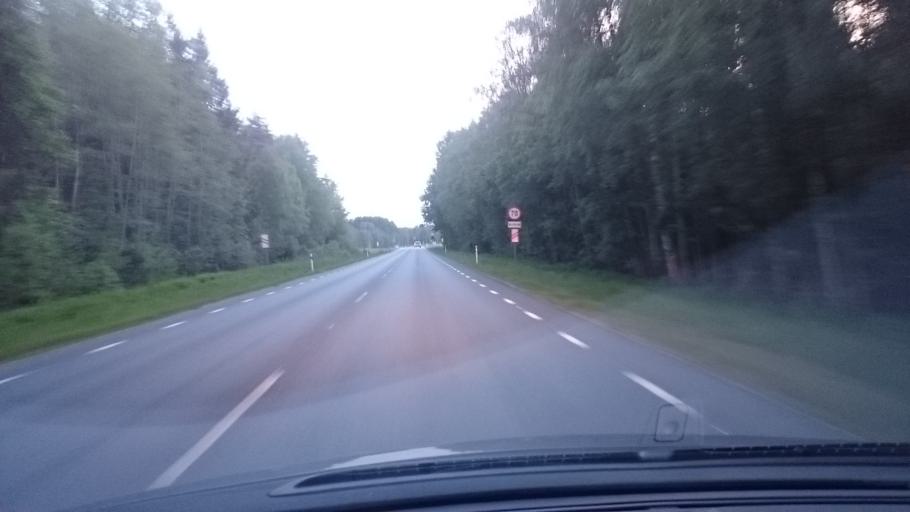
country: EE
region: Raplamaa
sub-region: Kehtna vald
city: Kehtna
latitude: 58.8530
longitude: 25.0153
